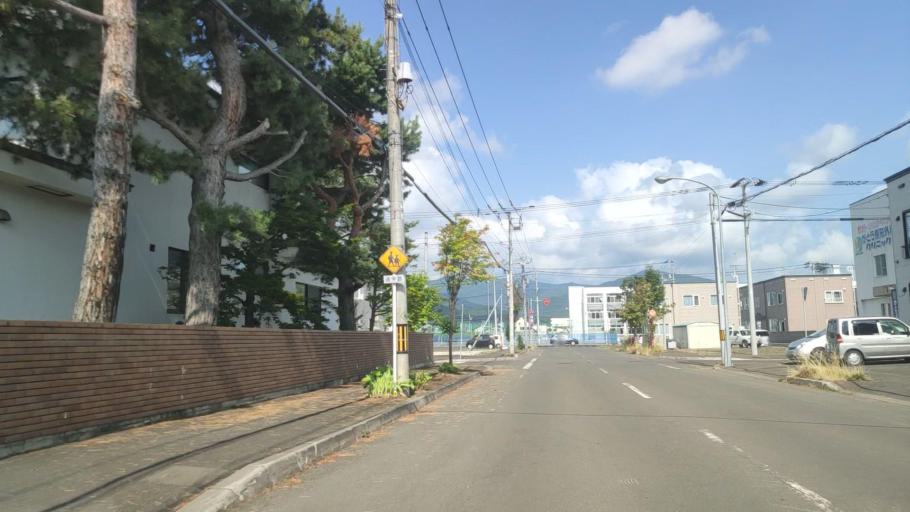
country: JP
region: Hokkaido
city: Shimo-furano
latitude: 43.3473
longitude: 142.3853
